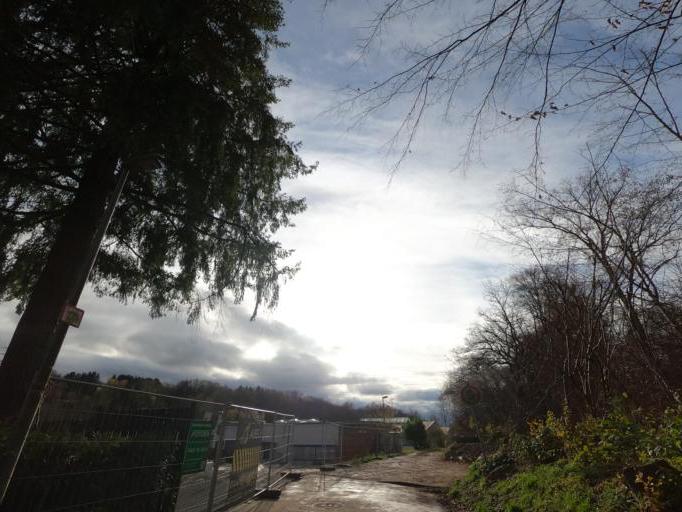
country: DE
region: Baden-Wuerttemberg
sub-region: Regierungsbezirk Stuttgart
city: Uhingen
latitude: 48.7035
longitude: 9.5729
